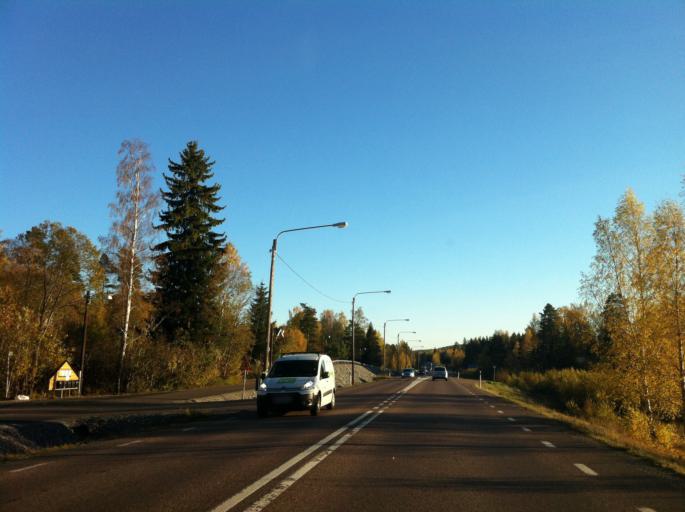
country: SE
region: Dalarna
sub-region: Faluns Kommun
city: Grycksbo
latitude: 60.6663
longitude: 15.5442
